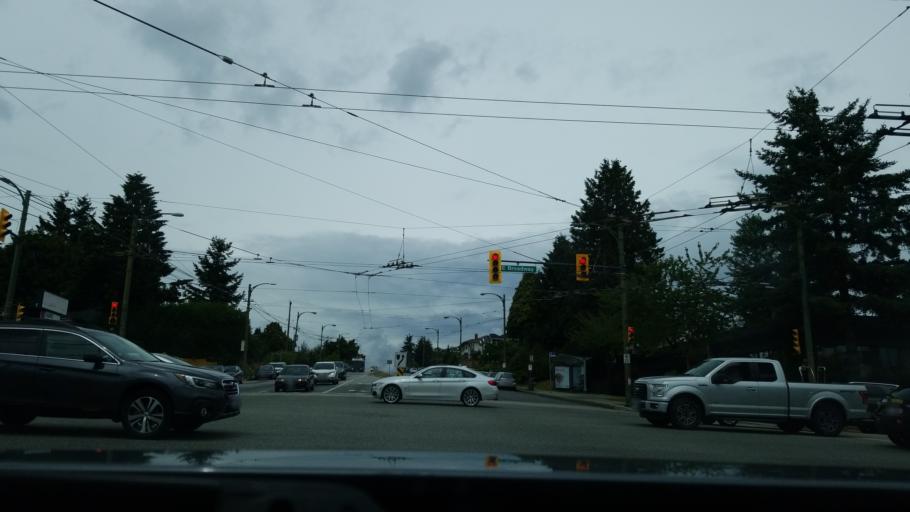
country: CA
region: British Columbia
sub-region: Fraser Valley Regional District
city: North Vancouver
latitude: 49.2618
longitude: -123.0443
